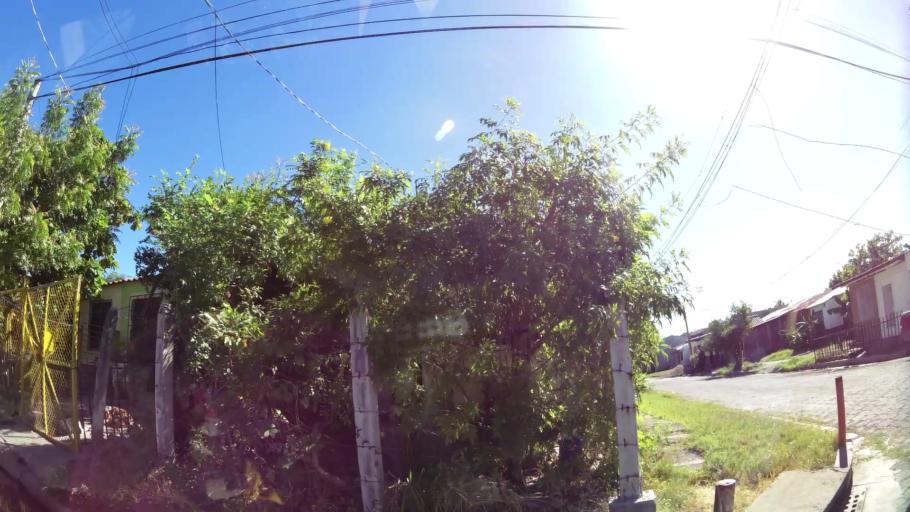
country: SV
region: San Miguel
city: San Miguel
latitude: 13.4706
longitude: -88.1571
